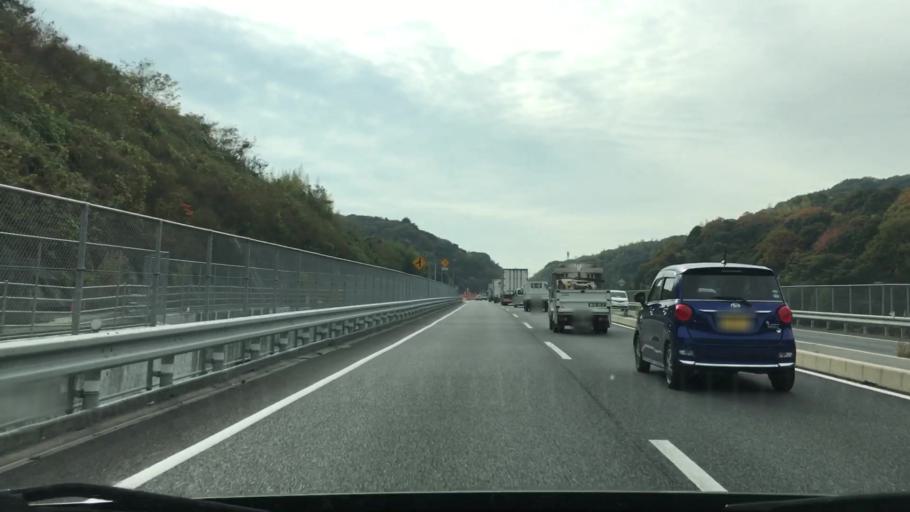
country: JP
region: Yamaguchi
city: Hofu
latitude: 34.0703
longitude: 131.6721
